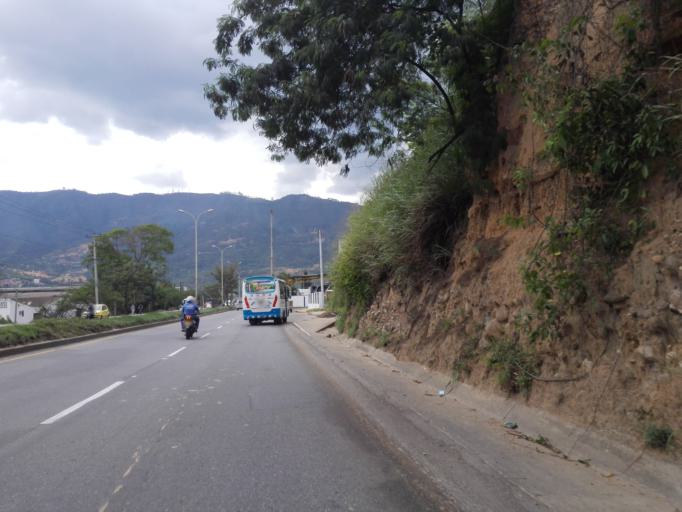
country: CO
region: Santander
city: Giron
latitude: 7.0848
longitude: -73.1610
